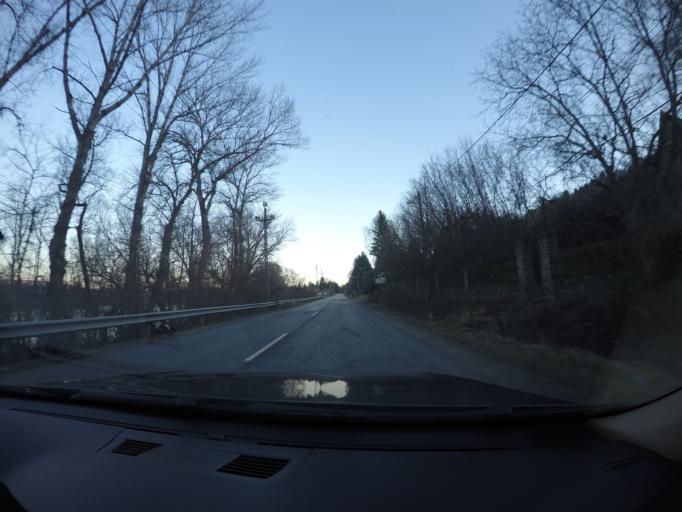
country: HU
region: Pest
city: Kismaros
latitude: 47.8042
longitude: 19.0043
